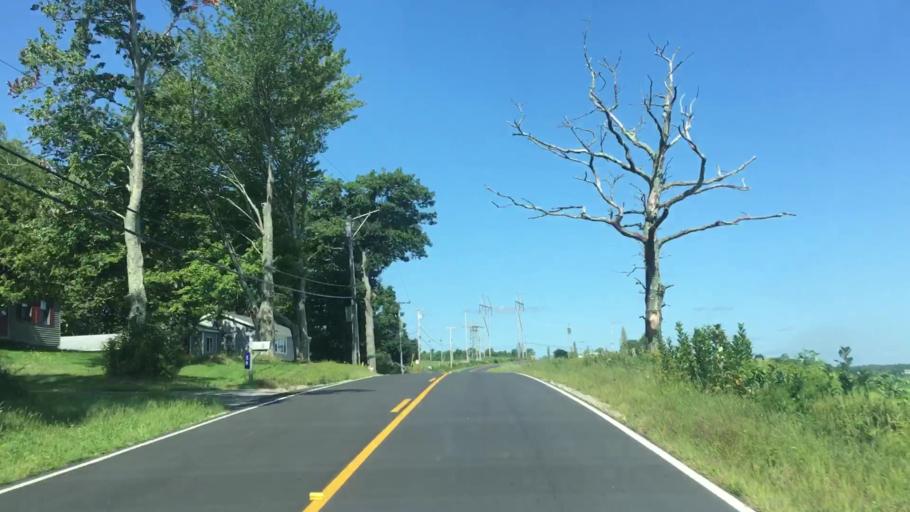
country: US
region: Maine
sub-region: Sagadahoc County
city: Topsham
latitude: 43.9570
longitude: -69.9745
